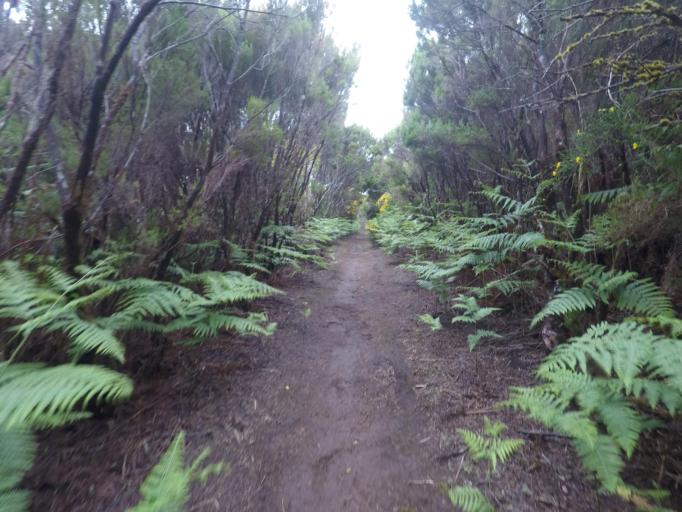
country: PT
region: Madeira
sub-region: Calheta
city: Arco da Calheta
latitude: 32.7782
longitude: -17.1326
